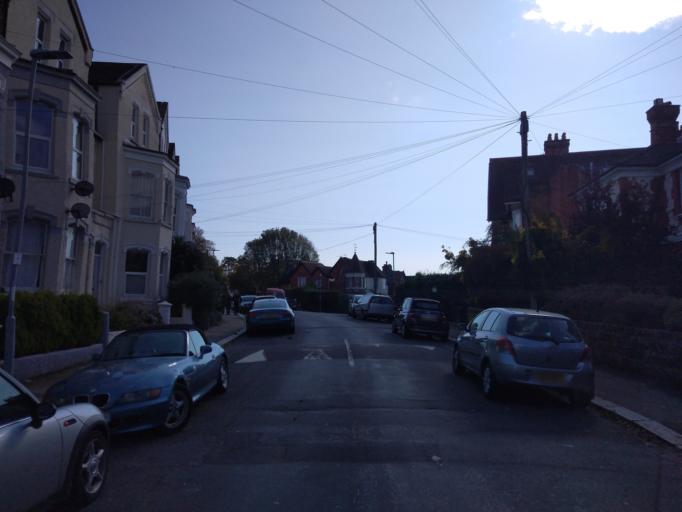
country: GB
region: England
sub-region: East Sussex
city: Hastings
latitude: 50.8614
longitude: 0.5593
